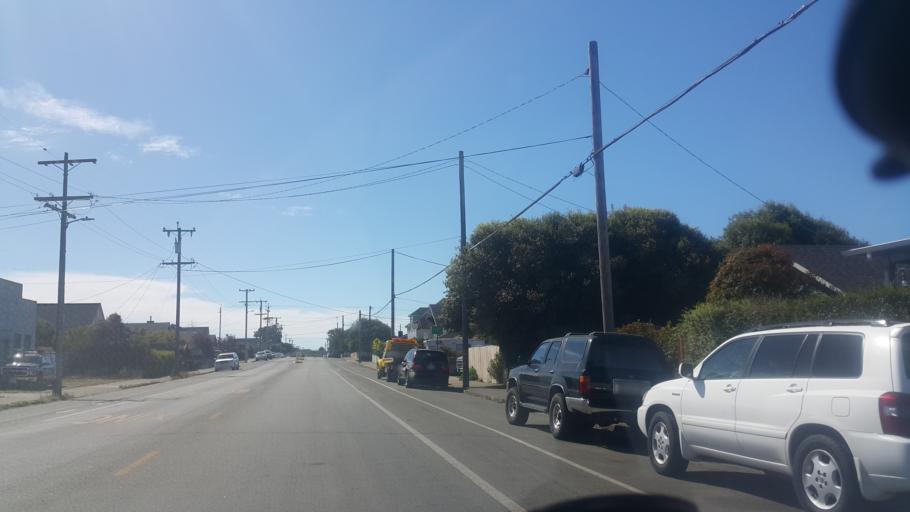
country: US
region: California
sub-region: Mendocino County
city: Fort Bragg
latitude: 39.4452
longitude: -123.7981
